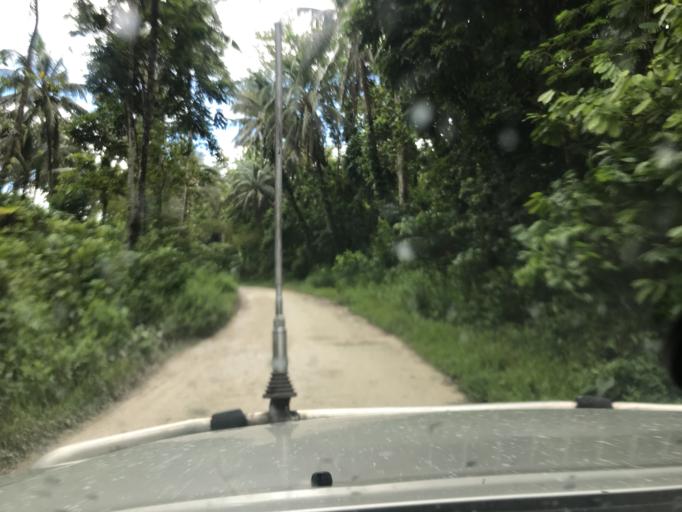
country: SB
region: Malaita
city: Auki
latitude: -8.4161
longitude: 160.6042
